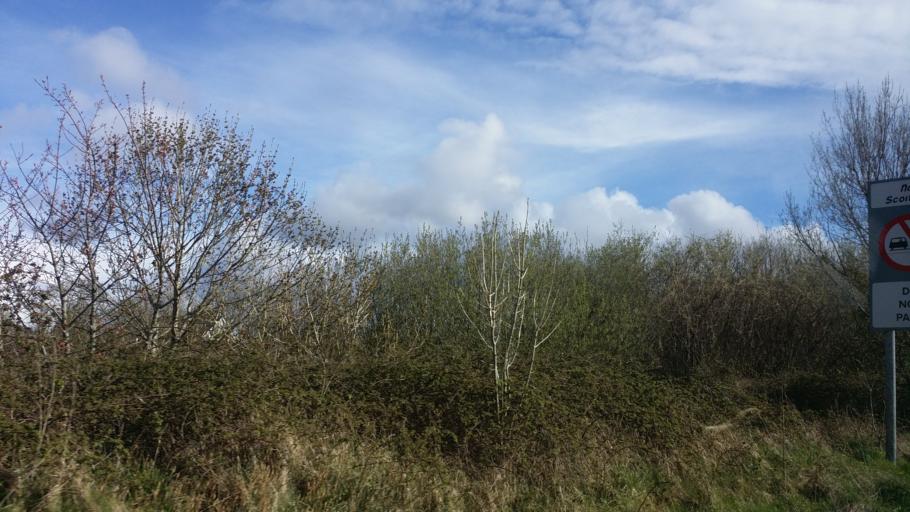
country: IE
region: Ulster
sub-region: County Donegal
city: Bundoran
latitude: 54.4691
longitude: -8.2773
